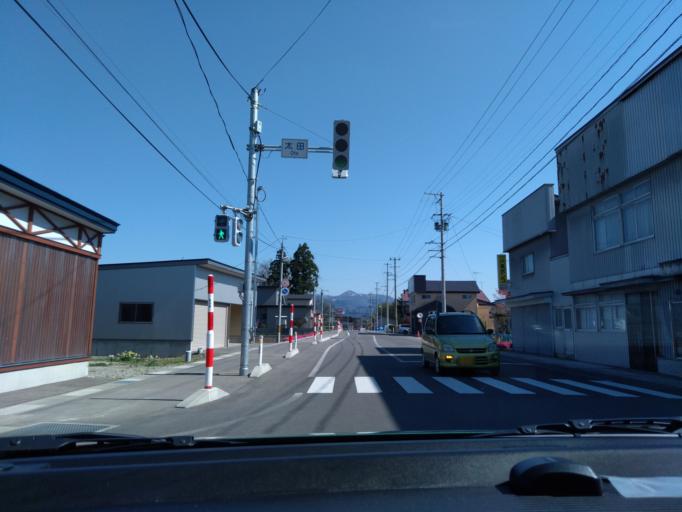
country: JP
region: Akita
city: Kakunodatemachi
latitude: 39.5121
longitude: 140.5926
